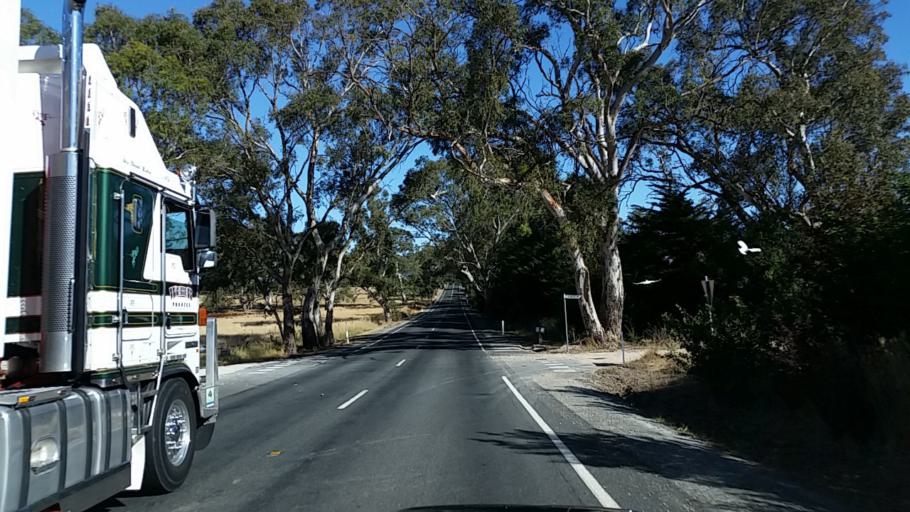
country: AU
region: South Australia
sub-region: Adelaide Hills
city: Birdwood
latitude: -34.7738
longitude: 139.0288
